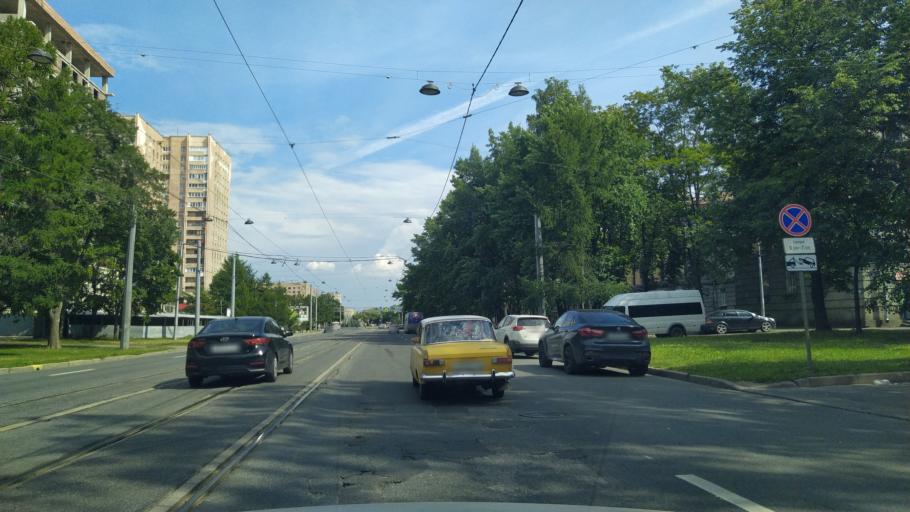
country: RU
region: St.-Petersburg
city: Kushelevka
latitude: 59.9992
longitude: 30.3571
